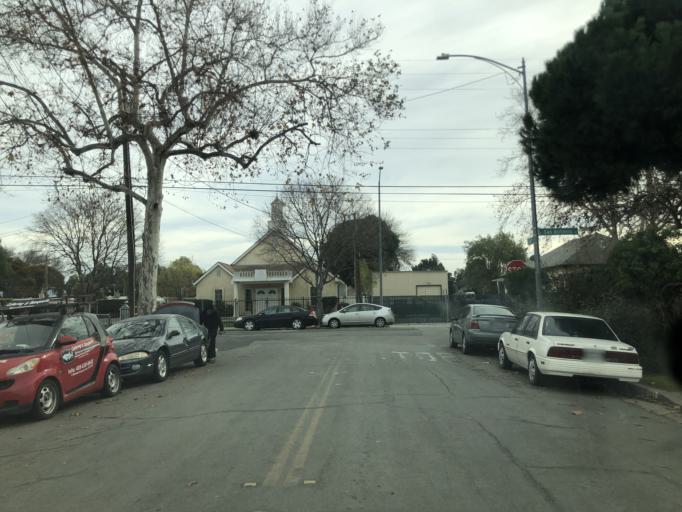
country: US
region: California
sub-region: Santa Clara County
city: San Jose
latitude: 37.3450
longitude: -121.8637
